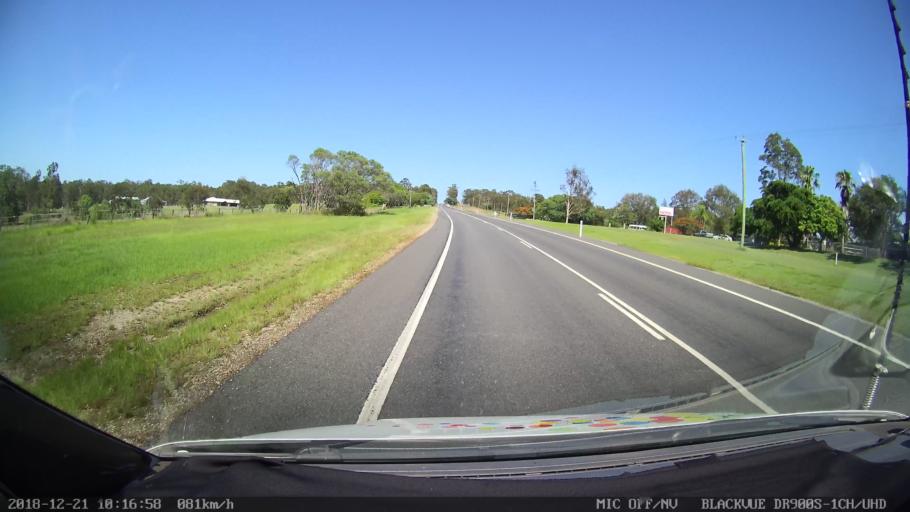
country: AU
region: New South Wales
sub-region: Clarence Valley
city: South Grafton
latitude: -29.6828
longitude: 152.8771
